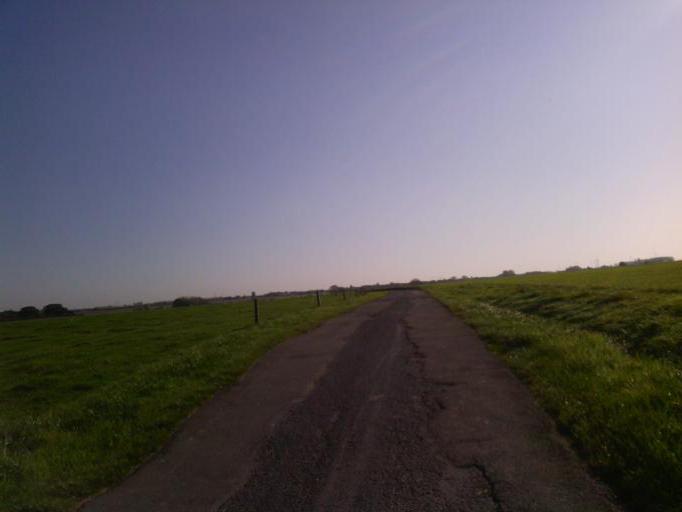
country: BE
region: Wallonia
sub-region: Province du Hainaut
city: Peruwelz
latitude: 50.5850
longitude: 3.5543
